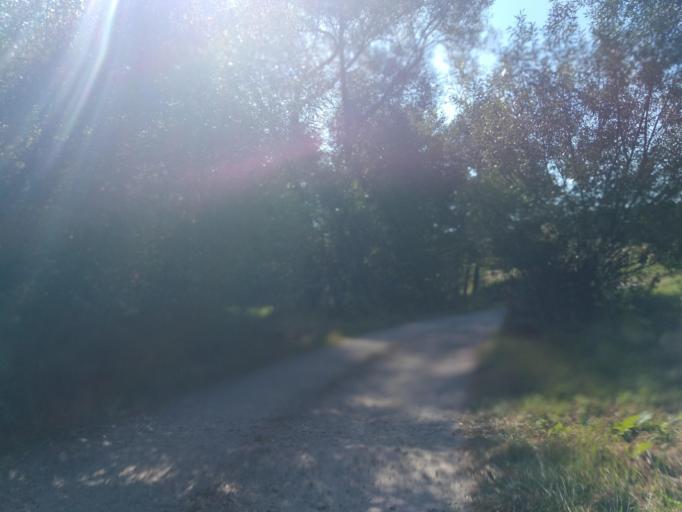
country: PL
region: Subcarpathian Voivodeship
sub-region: Powiat brzozowski
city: Brzozow
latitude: 49.7076
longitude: 22.0488
